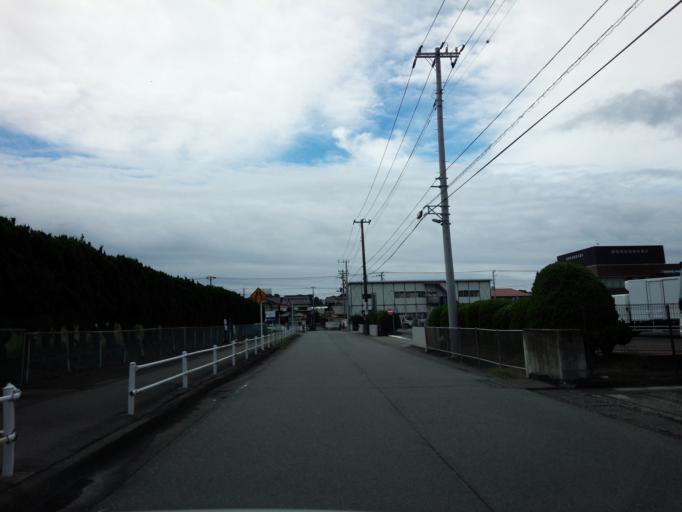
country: JP
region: Shizuoka
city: Numazu
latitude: 35.1319
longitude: 138.7810
